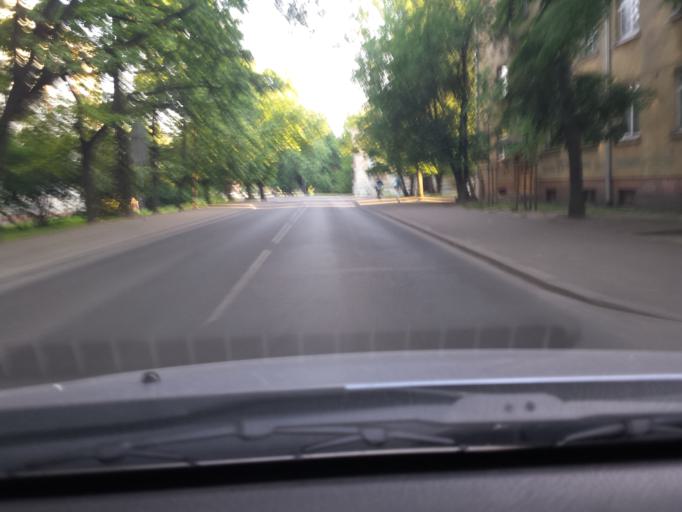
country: LV
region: Riga
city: Jaunciems
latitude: 56.9682
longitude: 24.1773
